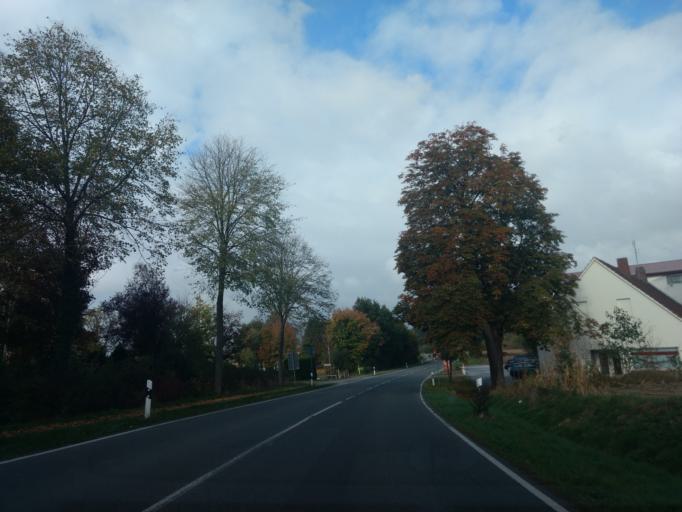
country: DE
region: Lower Saxony
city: Hilter
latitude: 52.1365
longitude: 8.1127
